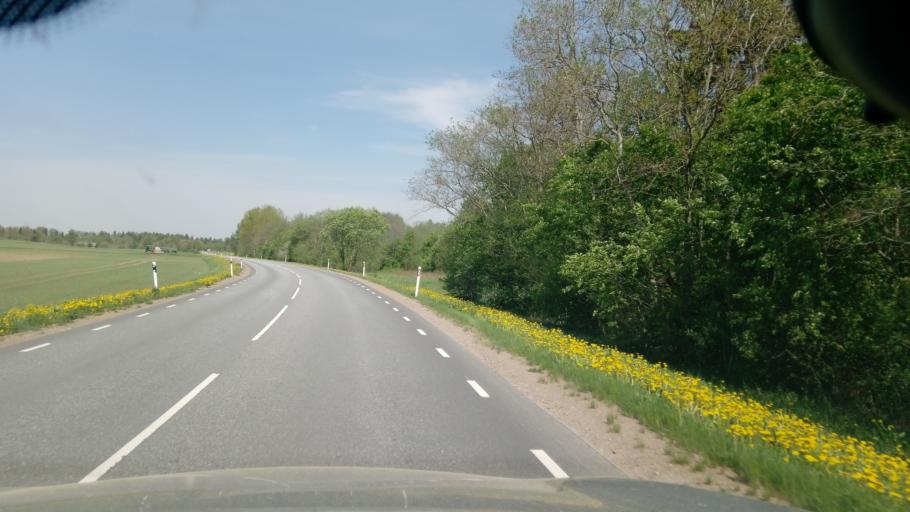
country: EE
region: Laeaene-Virumaa
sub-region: Tapa vald
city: Tapa
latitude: 59.3469
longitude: 26.0058
